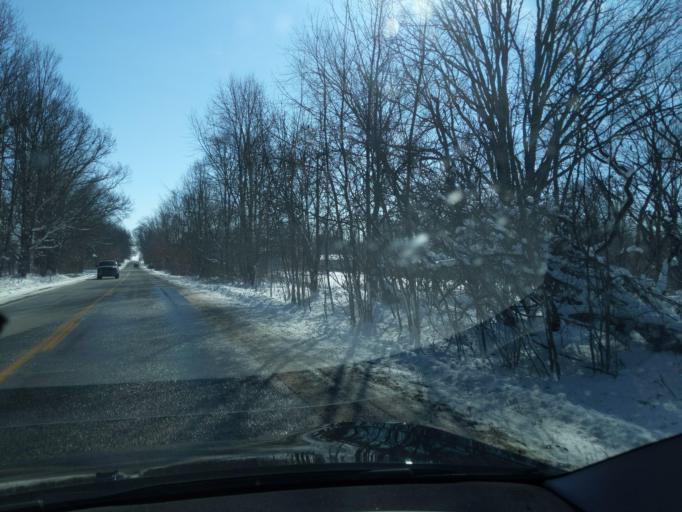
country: US
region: Michigan
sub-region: Livingston County
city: Fowlerville
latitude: 42.5732
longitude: -84.0723
